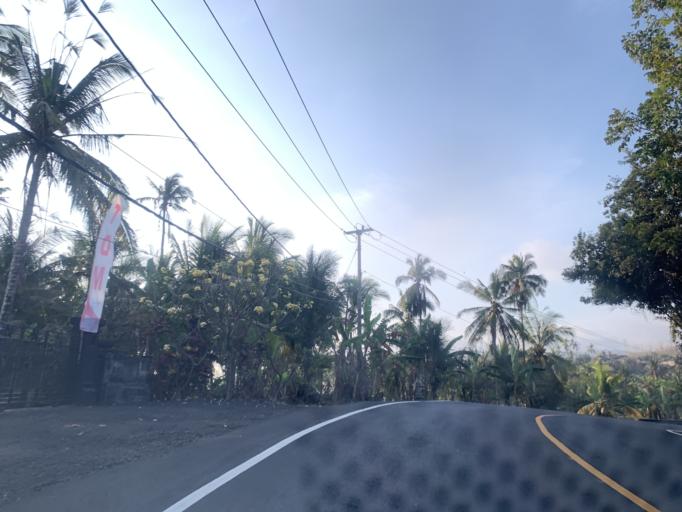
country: ID
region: Bali
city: Angkahgede
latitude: -8.4802
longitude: 114.9403
